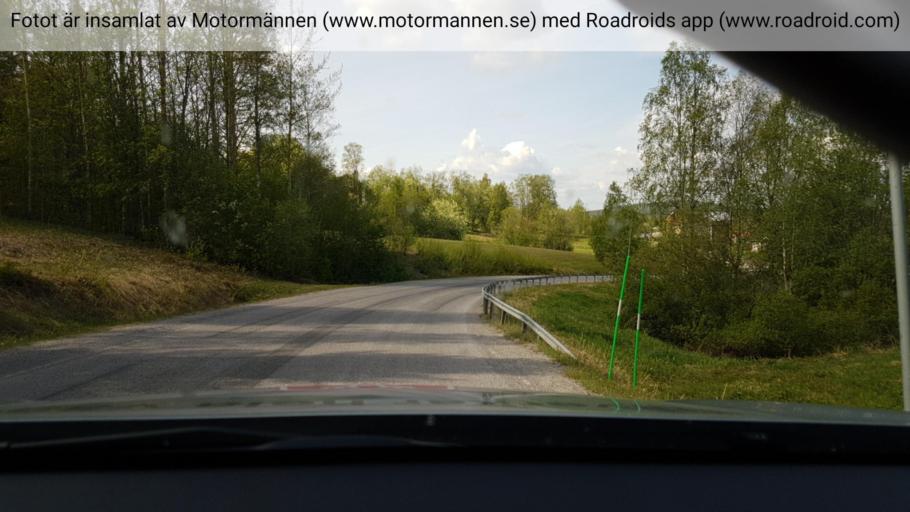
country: SE
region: Vaesterbotten
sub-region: Umea Kommun
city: Roback
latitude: 63.8728
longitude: 20.0433
